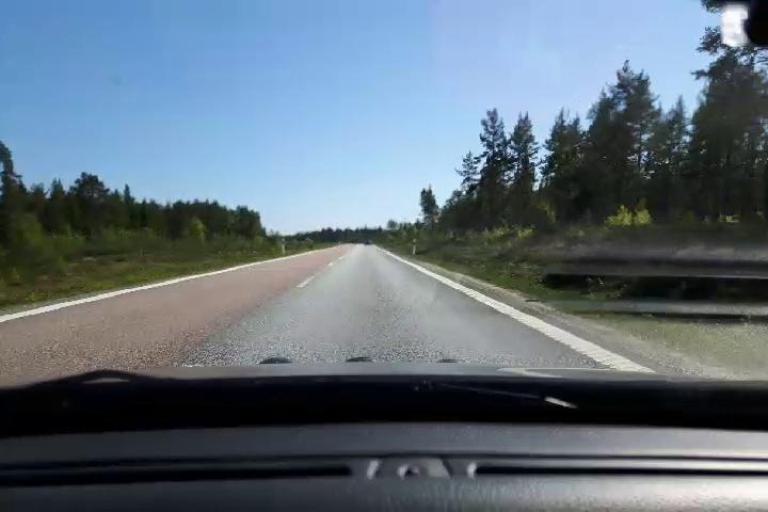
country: SE
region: Gaevleborg
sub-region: Soderhamns Kommun
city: Soderhamn
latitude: 61.3899
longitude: 16.9921
